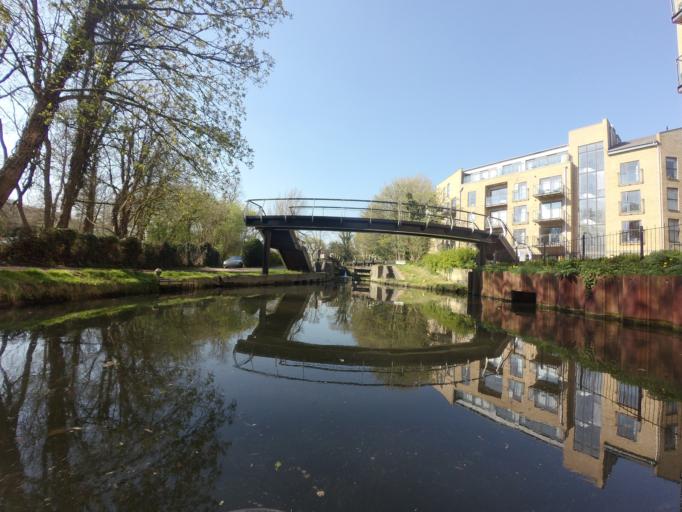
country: GB
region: England
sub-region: Hertfordshire
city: Kings Langley
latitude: 51.7293
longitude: -0.4536
